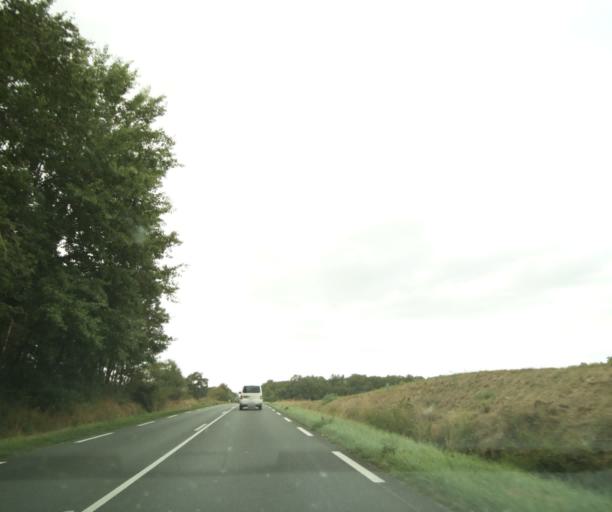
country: FR
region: Centre
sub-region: Departement d'Indre-et-Loire
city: Chambourg-sur-Indre
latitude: 47.1738
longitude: 0.9747
